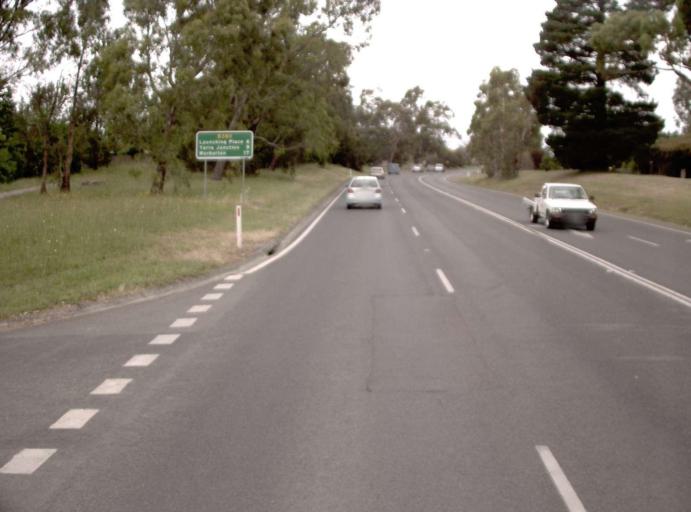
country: AU
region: Victoria
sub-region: Yarra Ranges
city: Woori Yallock
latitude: -37.7803
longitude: 145.5344
